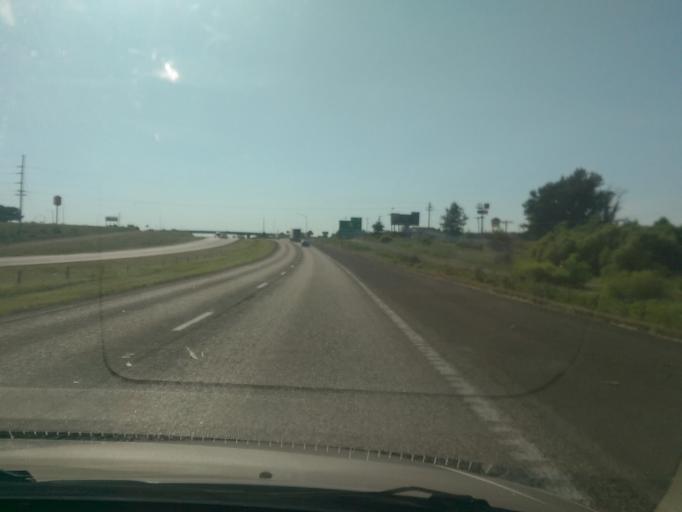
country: US
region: Missouri
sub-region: Lafayette County
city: Higginsville
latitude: 39.0003
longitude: -93.7291
